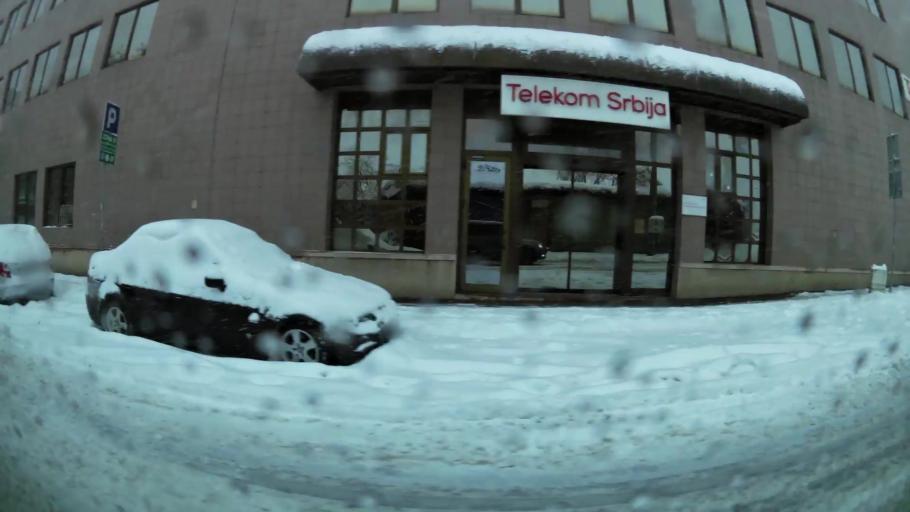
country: RS
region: Central Serbia
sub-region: Belgrade
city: Stari Grad
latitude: 44.8278
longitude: 20.4624
